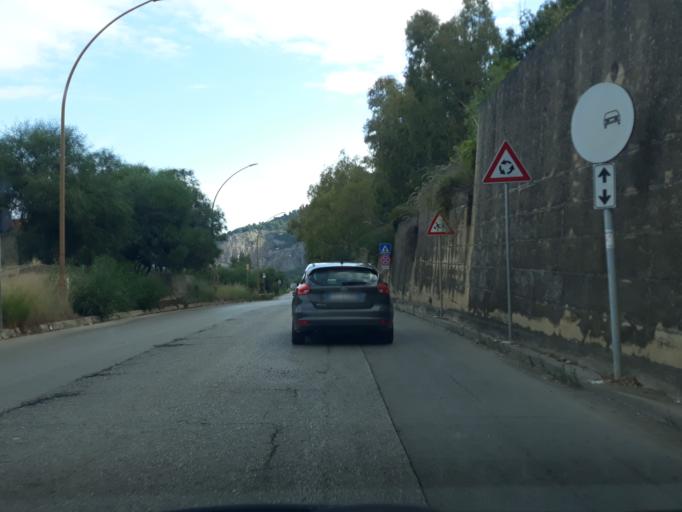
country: IT
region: Sicily
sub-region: Palermo
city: Cefalu
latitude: 38.0270
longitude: 14.0161
